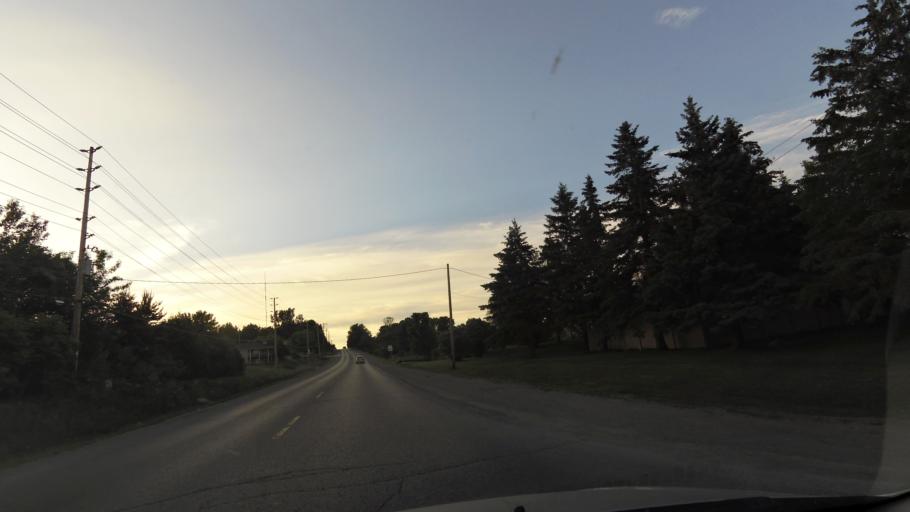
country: CA
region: Ontario
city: Peterborough
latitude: 44.3153
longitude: -78.2897
